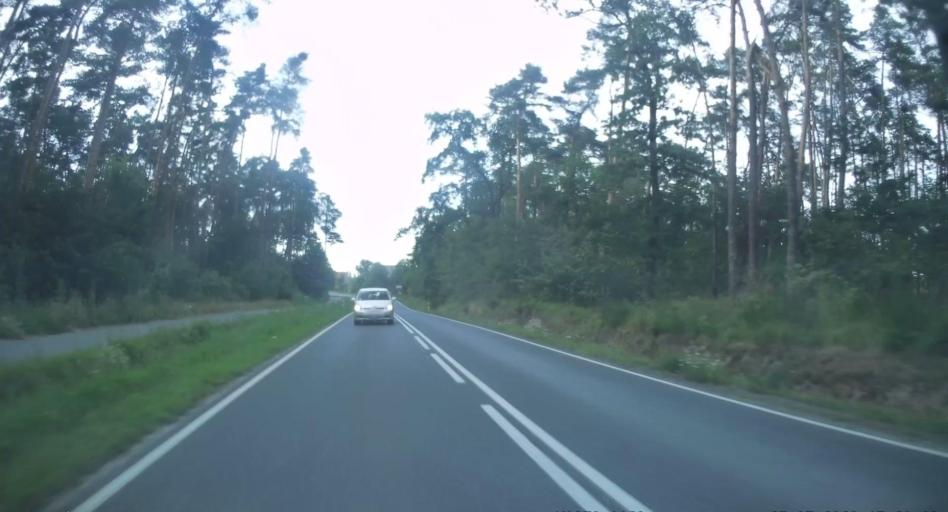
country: PL
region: Lesser Poland Voivodeship
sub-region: Powiat brzeski
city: Przyborow
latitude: 50.0565
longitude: 20.6395
